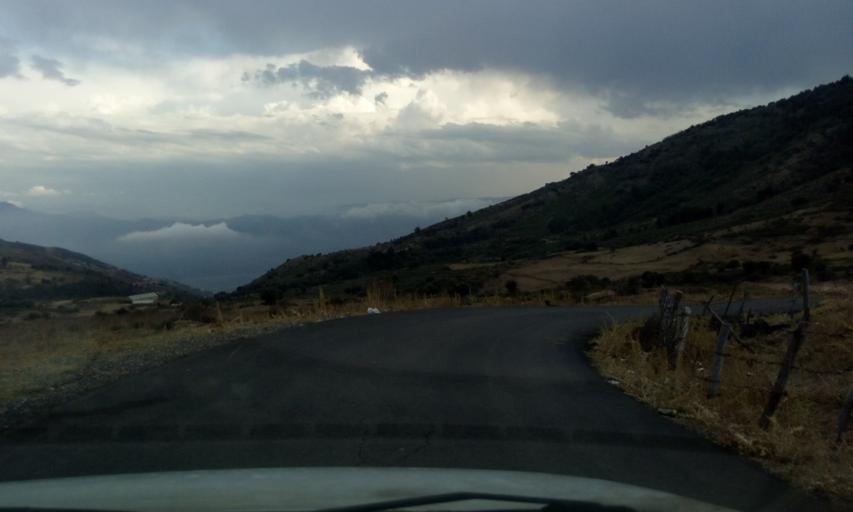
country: DZ
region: Tizi Ouzou
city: Chemini
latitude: 36.6117
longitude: 4.5586
